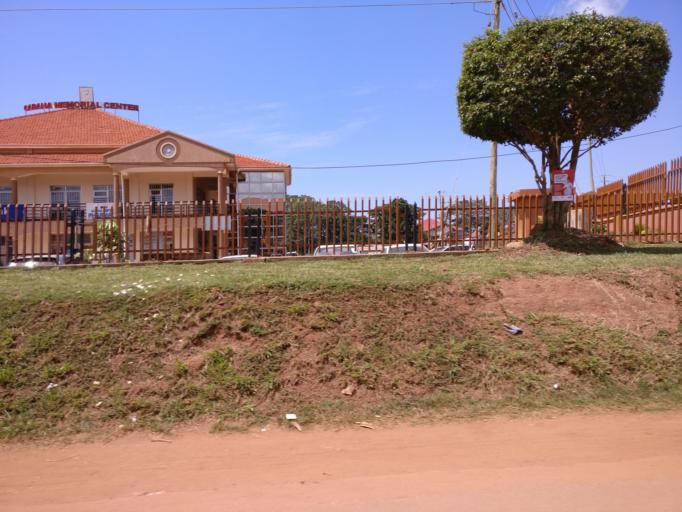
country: UG
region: Central Region
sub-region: Wakiso District
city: Kajansi
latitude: 0.1379
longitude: 32.5385
